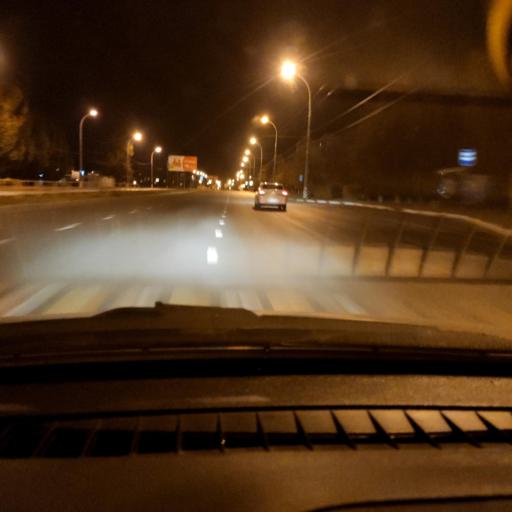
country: RU
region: Samara
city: Tol'yatti
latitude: 53.5038
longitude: 49.2910
